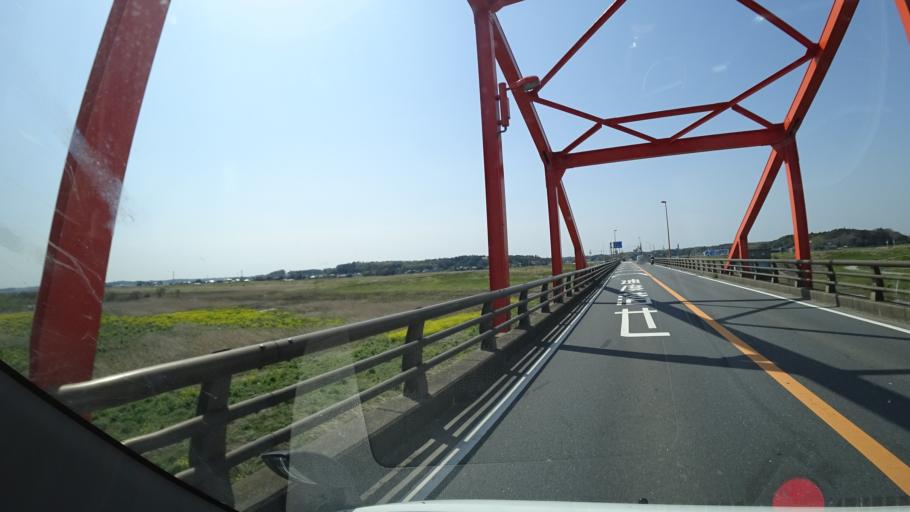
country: JP
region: Ibaraki
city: Edosaki
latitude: 35.8699
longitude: 140.2893
